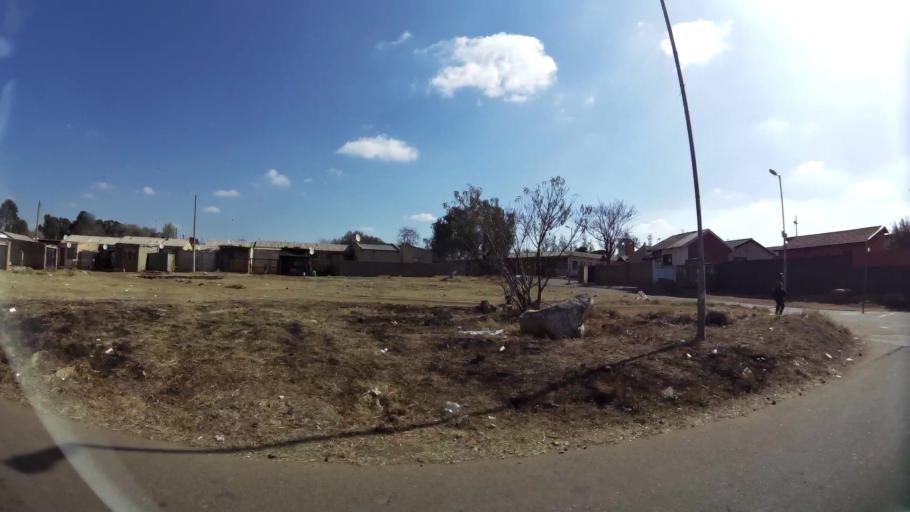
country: ZA
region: Gauteng
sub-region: City of Johannesburg Metropolitan Municipality
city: Soweto
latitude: -26.2568
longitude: 27.8880
